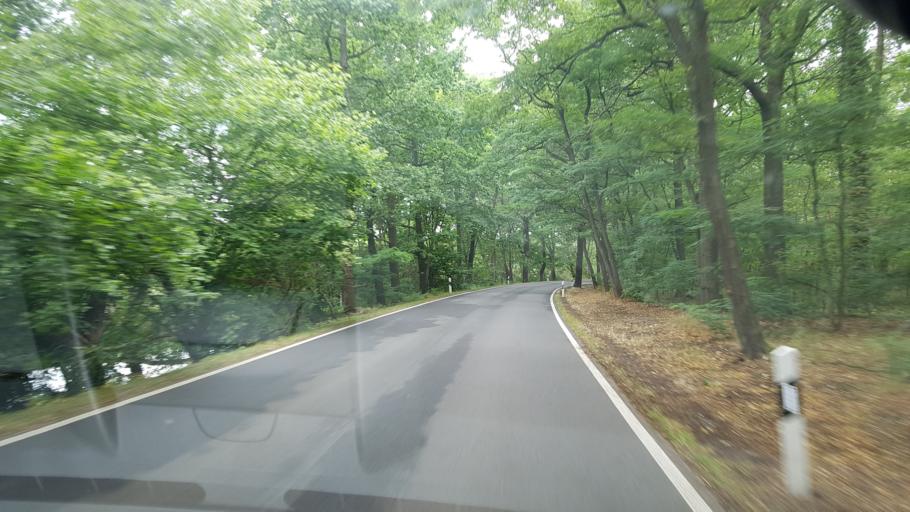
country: DE
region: Saxony
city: Mucka
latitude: 51.3804
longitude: 14.6755
